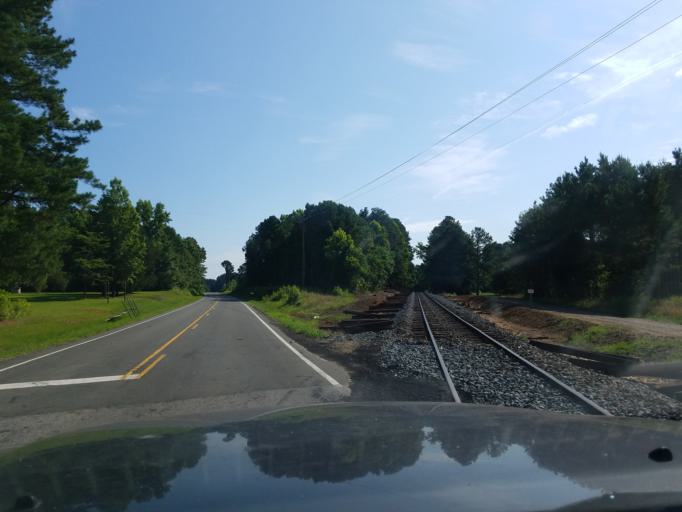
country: US
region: North Carolina
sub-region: Granville County
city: Oxford
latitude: 36.2715
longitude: -78.6459
